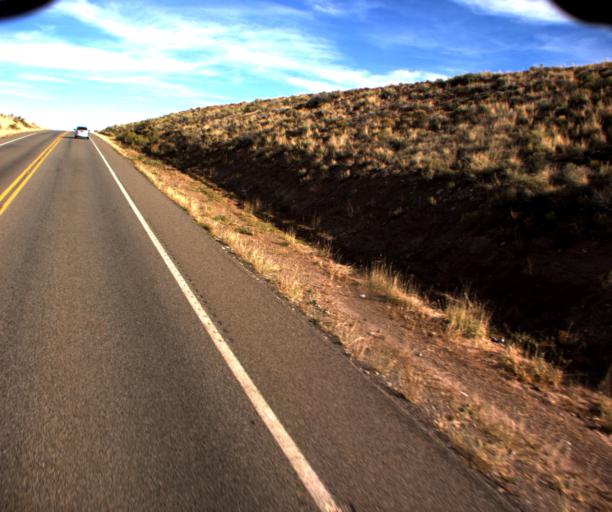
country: US
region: Arizona
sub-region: Apache County
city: Lukachukai
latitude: 36.9278
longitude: -109.1938
